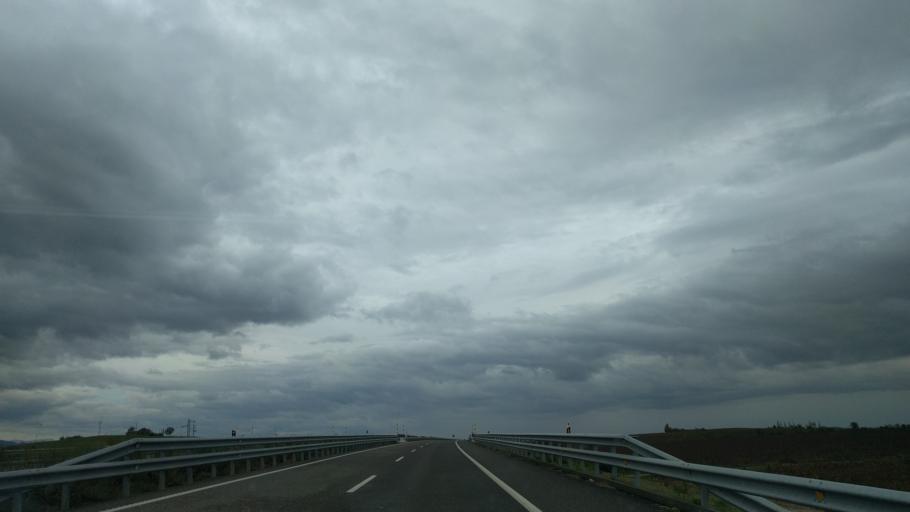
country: ES
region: Aragon
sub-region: Provincia de Huesca
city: Castejon del Puente
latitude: 41.9881
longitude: 0.1193
